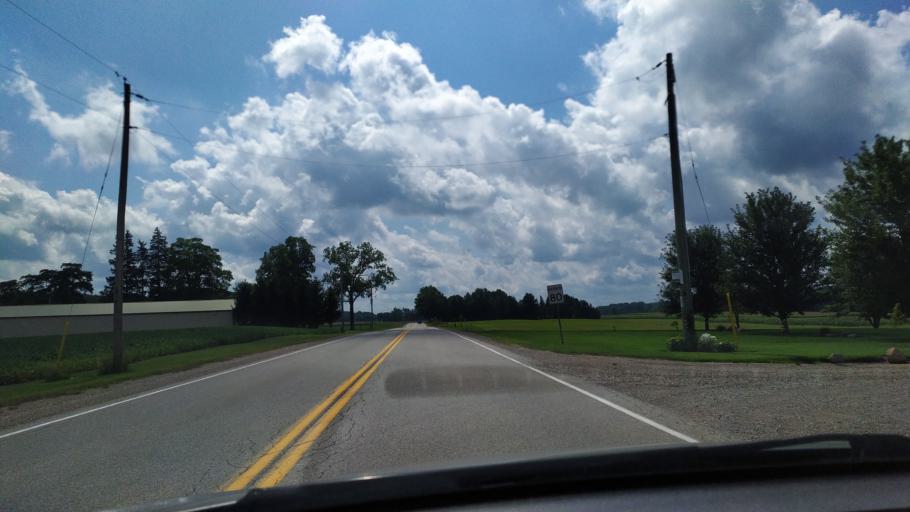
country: CA
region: Ontario
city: London
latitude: 43.0652
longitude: -81.3347
